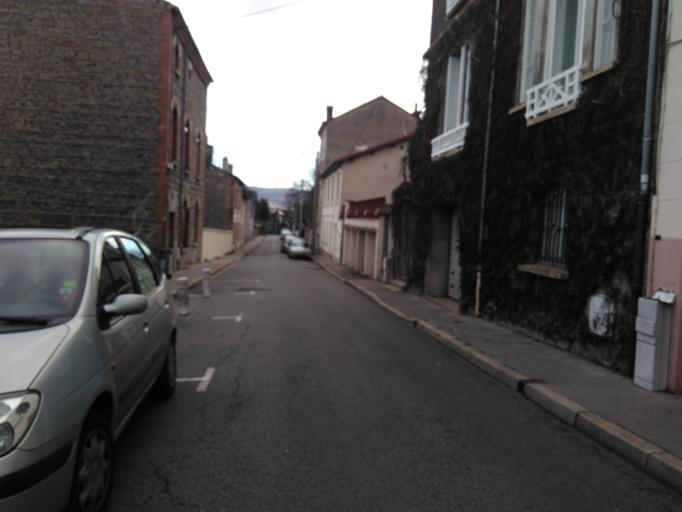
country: FR
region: Rhone-Alpes
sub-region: Departement de la Loire
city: Saint-Priest-en-Jarez
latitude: 45.4580
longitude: 4.3801
